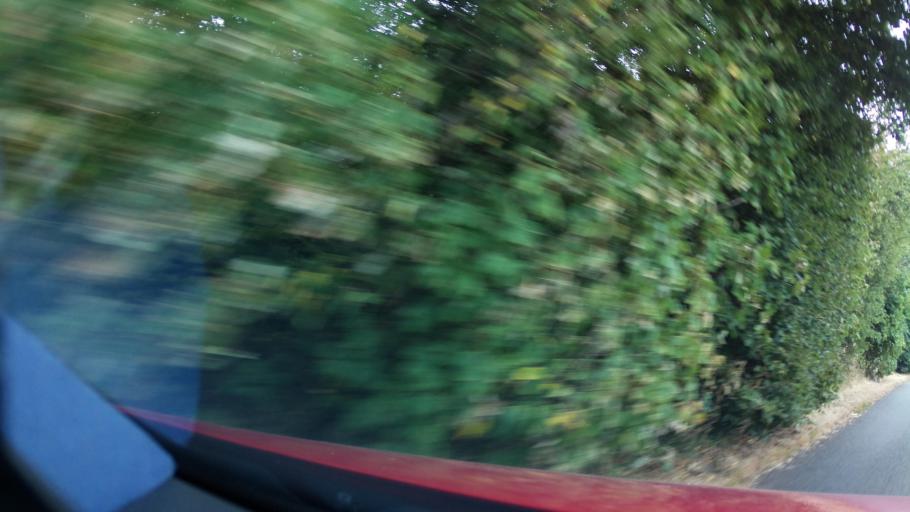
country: GB
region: England
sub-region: Leicestershire
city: Ashby de la Zouch
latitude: 52.7372
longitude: -1.4886
